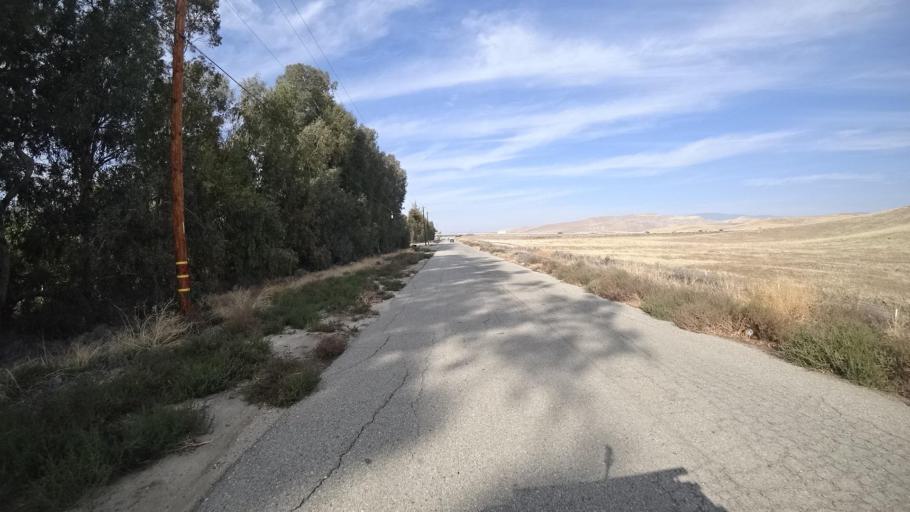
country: US
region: California
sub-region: Kern County
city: Arvin
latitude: 35.2888
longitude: -118.7527
